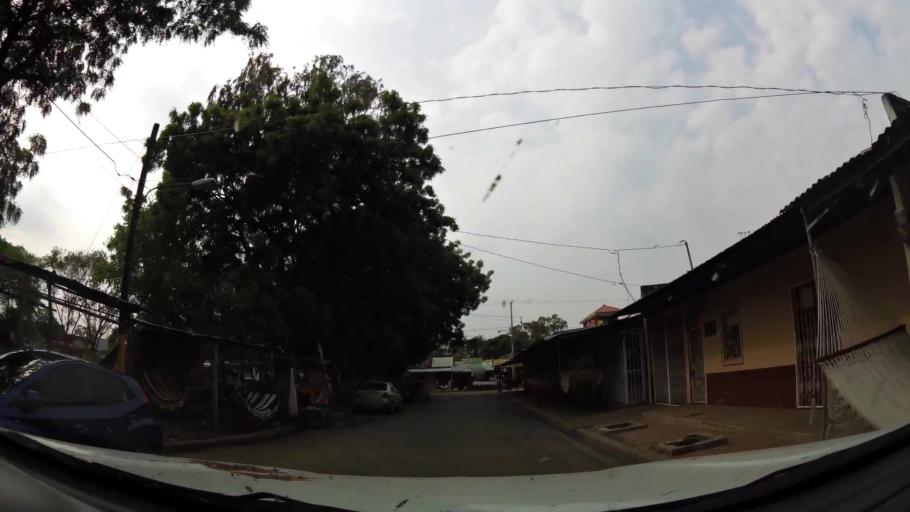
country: NI
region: Masaya
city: Masaya
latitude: 11.9741
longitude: -86.1031
